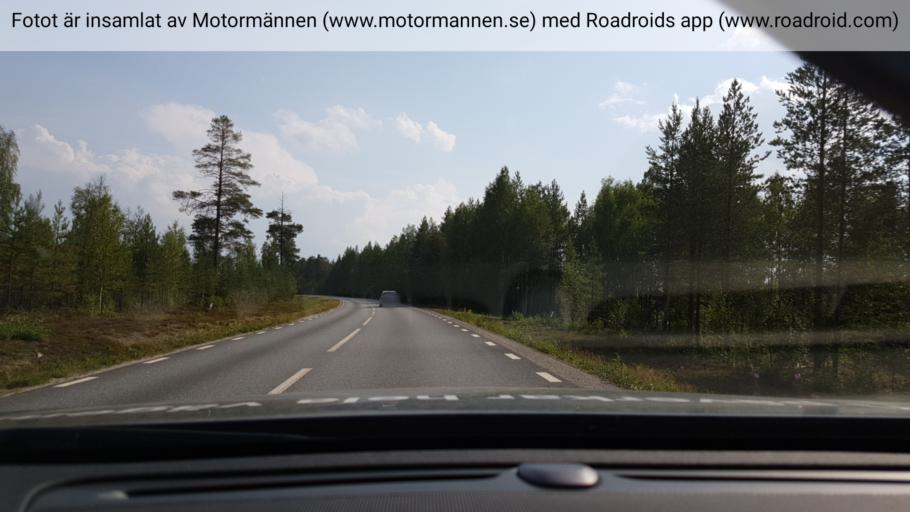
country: SE
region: Vaesterbotten
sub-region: Bjurholms Kommun
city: Bjurholm
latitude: 64.3390
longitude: 19.1458
